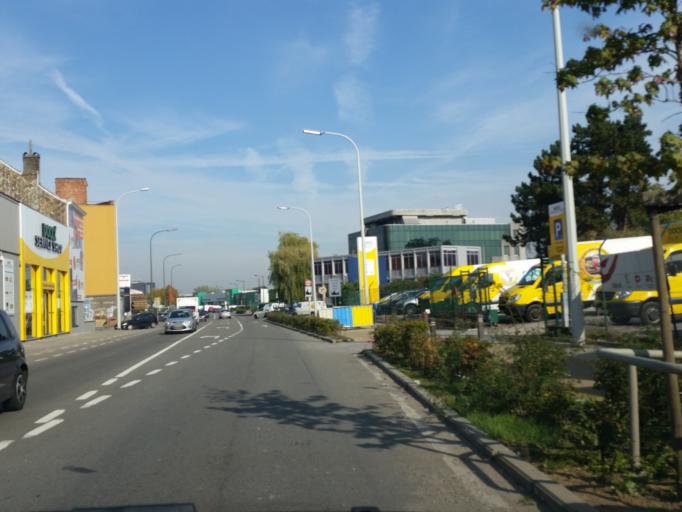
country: BE
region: Flanders
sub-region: Provincie Vlaams-Brabant
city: Drogenbos
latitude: 50.8114
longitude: 4.3059
